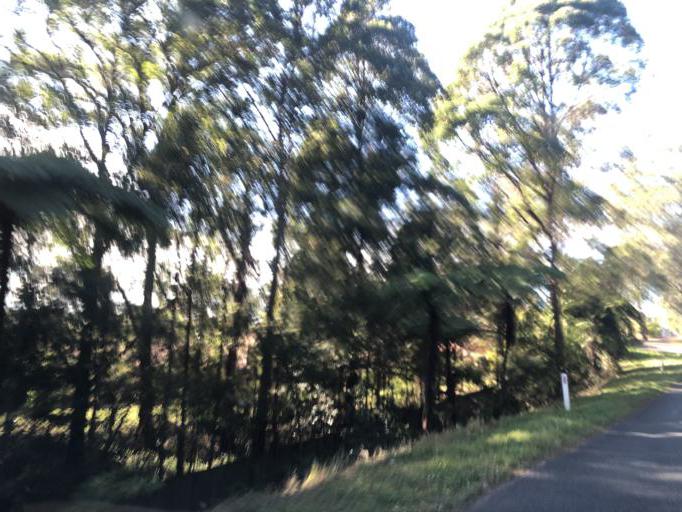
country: AU
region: New South Wales
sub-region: Coffs Harbour
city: Toormina
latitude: -30.3486
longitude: 153.0867
